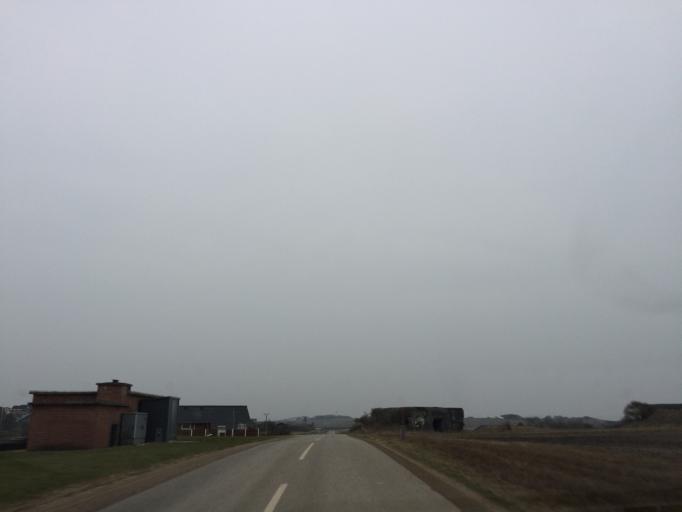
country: DK
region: Central Jutland
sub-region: Lemvig Kommune
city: Lemvig
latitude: 56.5813
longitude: 8.2743
